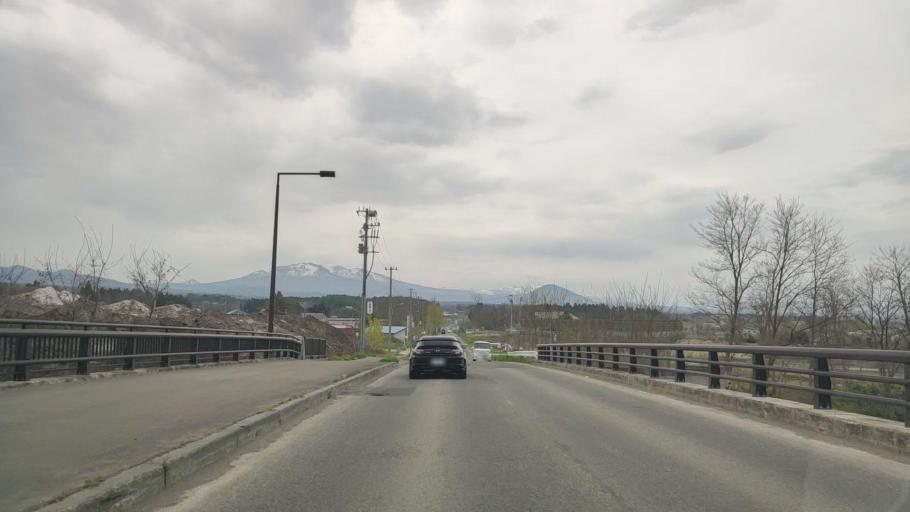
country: JP
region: Aomori
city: Aomori Shi
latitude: 40.7971
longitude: 140.7843
